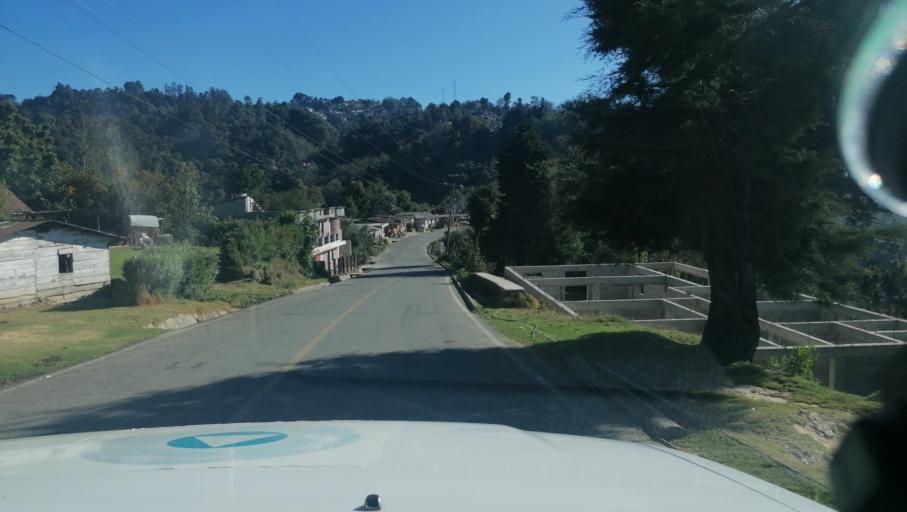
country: MX
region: Chiapas
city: Motozintla de Mendoza
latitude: 15.2530
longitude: -92.2191
